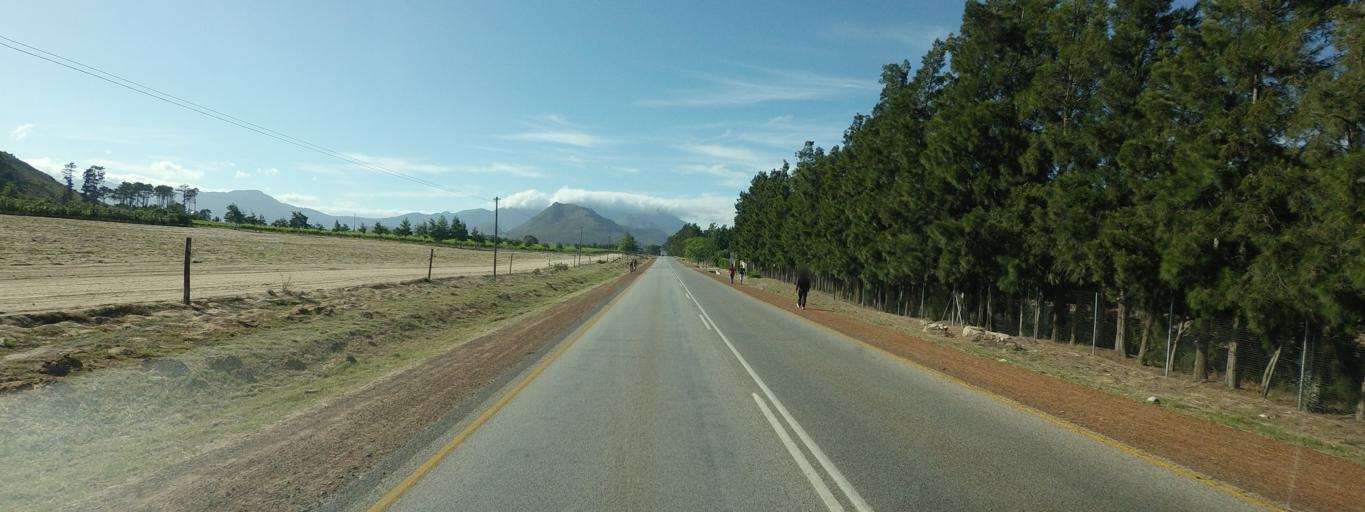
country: ZA
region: Western Cape
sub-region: Cape Winelands District Municipality
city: Paarl
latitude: -33.8642
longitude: 19.0401
